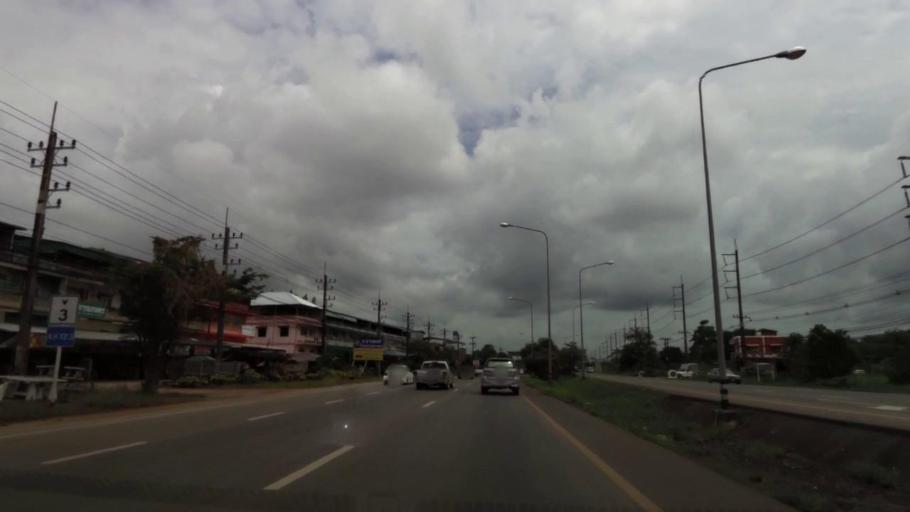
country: TH
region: Chanthaburi
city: Na Yai Am
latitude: 12.7612
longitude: 101.8554
